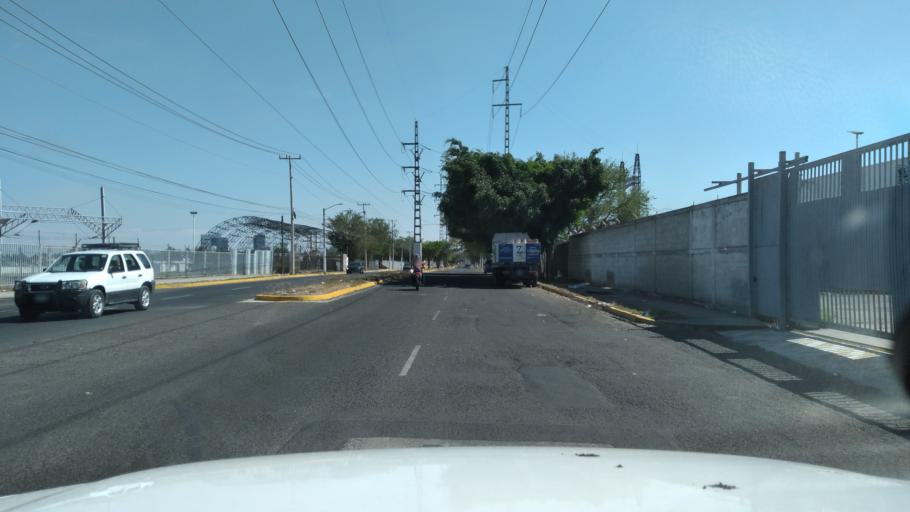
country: MX
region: Jalisco
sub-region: Zapopan
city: Zapopan
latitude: 20.7349
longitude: -103.3760
